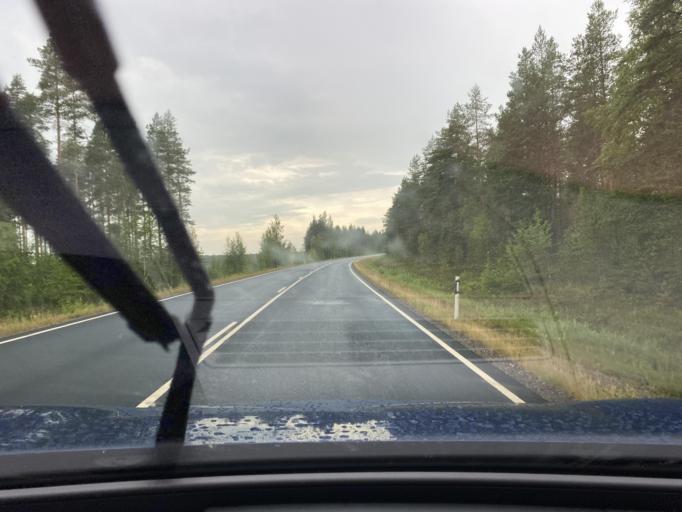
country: FI
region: Central Ostrobothnia
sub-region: Kaustinen
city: Veteli
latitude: 63.4104
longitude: 23.9621
